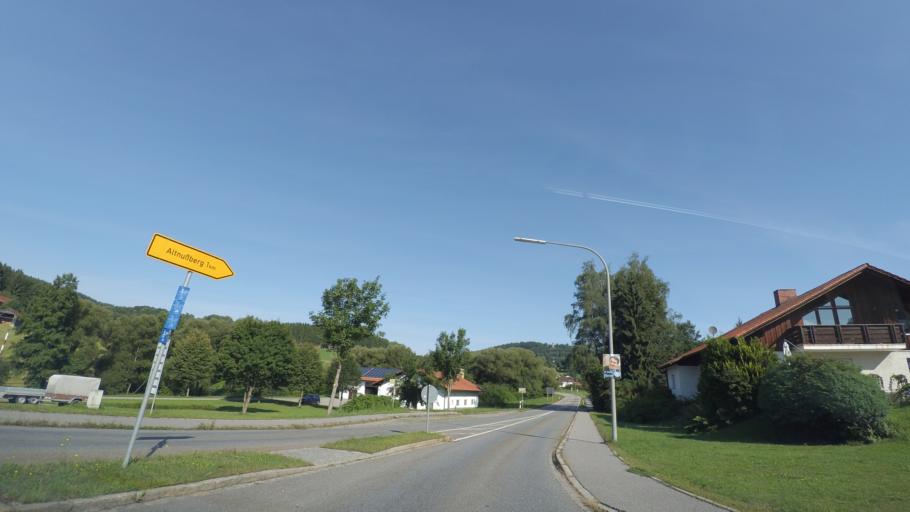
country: DE
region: Bavaria
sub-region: Lower Bavaria
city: Geiersthal
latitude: 49.0481
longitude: 12.9766
